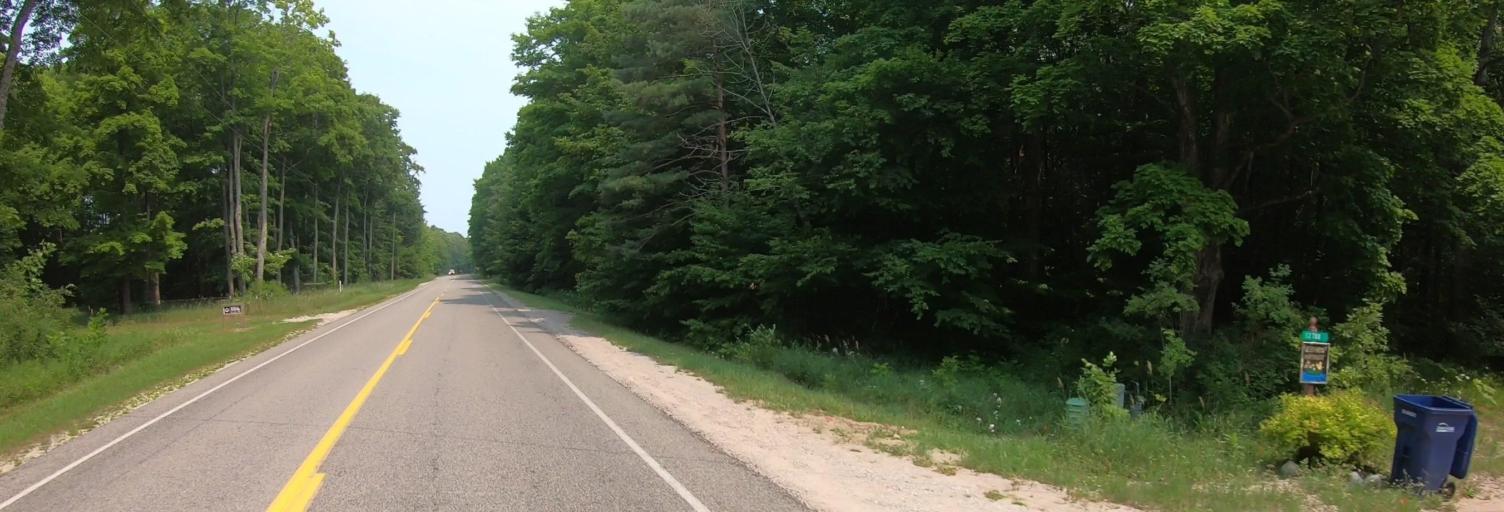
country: US
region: Michigan
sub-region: Leelanau County
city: Leland
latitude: 45.1556
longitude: -85.5905
